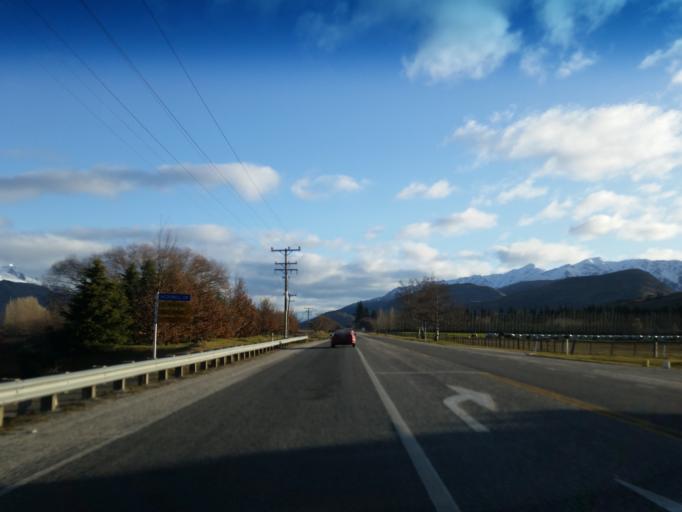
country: NZ
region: Otago
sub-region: Queenstown-Lakes District
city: Arrowtown
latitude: -44.9951
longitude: 168.7922
